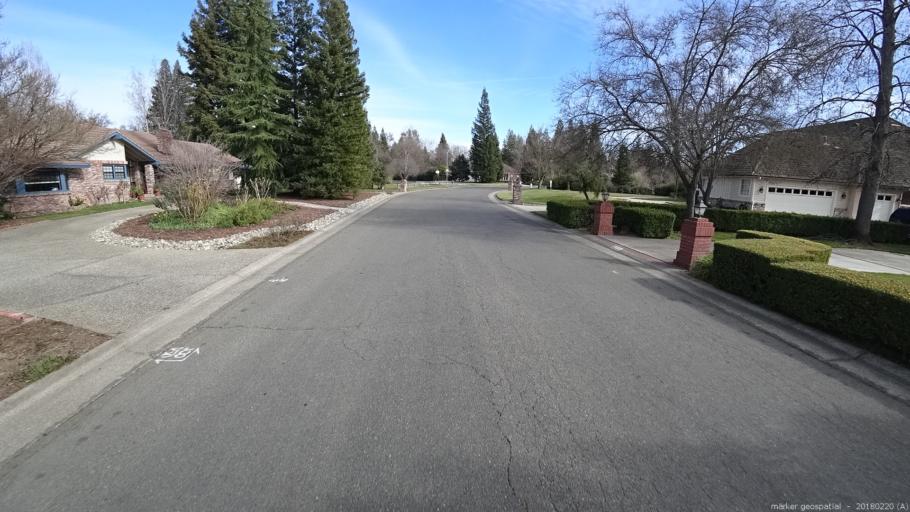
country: US
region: California
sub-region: Sacramento County
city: Orangevale
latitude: 38.7162
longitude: -121.2360
